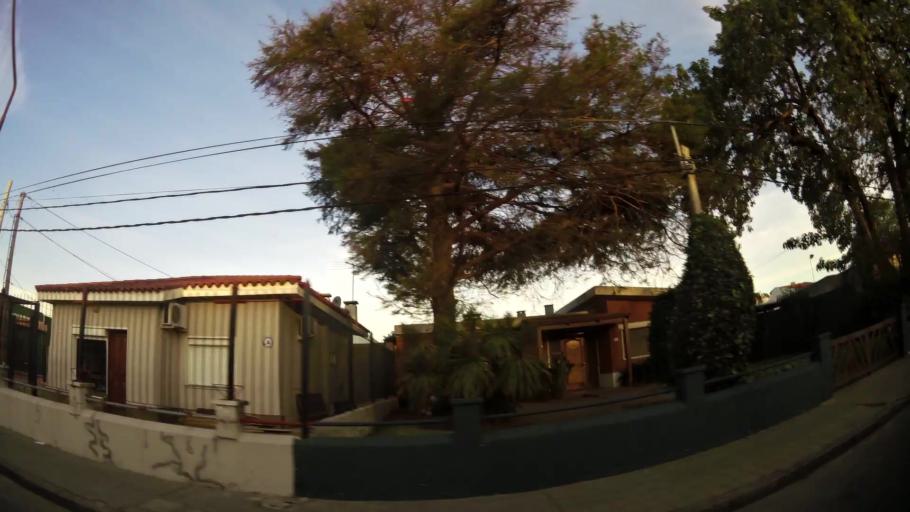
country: UY
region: Maldonado
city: Maldonado
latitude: -34.9120
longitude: -54.9532
